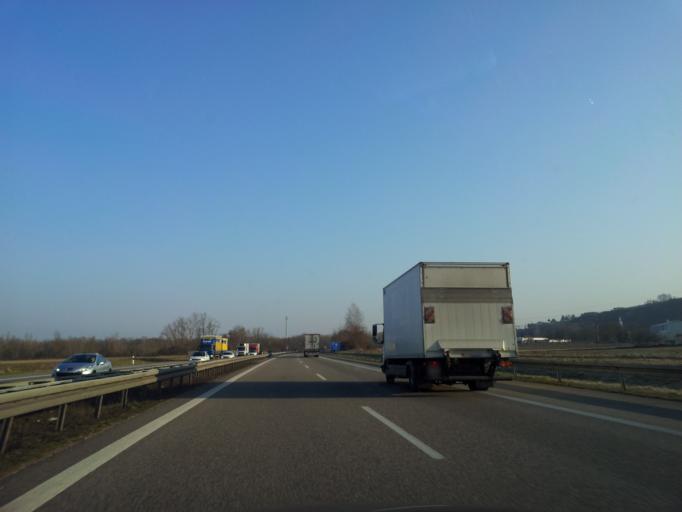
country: FR
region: Alsace
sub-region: Departement du Haut-Rhin
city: Kembs
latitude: 47.6988
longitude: 7.5212
